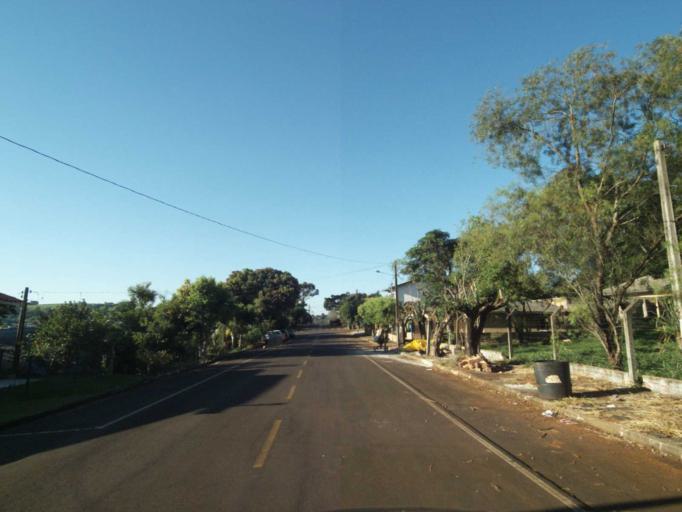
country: BR
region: Parana
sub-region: Coronel Vivida
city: Coronel Vivida
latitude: -25.9705
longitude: -52.8119
